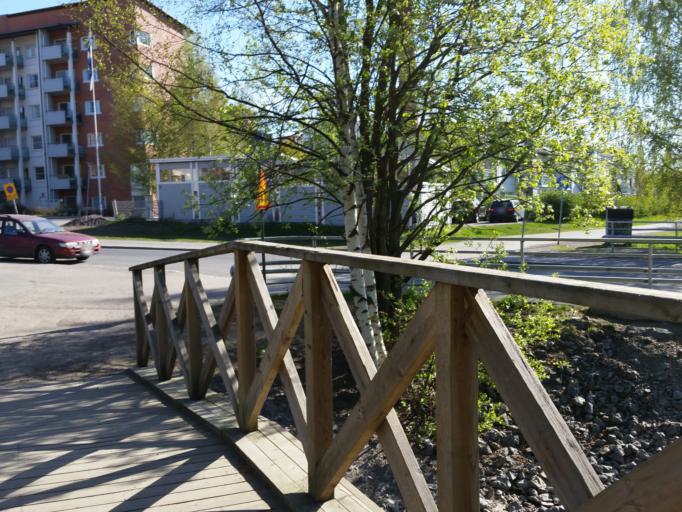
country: FI
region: Pirkanmaa
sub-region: Tampere
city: Tampere
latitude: 61.4899
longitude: 23.7858
